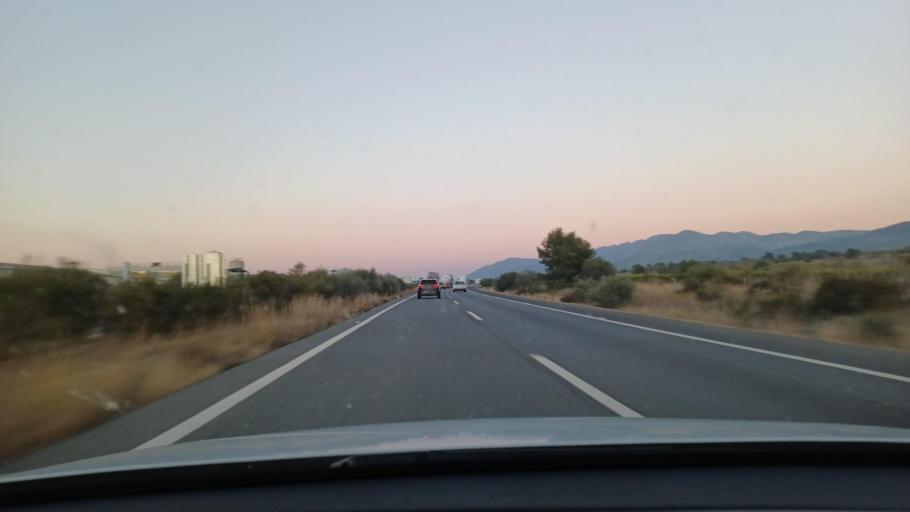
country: ES
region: Catalonia
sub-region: Provincia de Tarragona
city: Ulldecona
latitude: 40.5692
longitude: 0.4342
